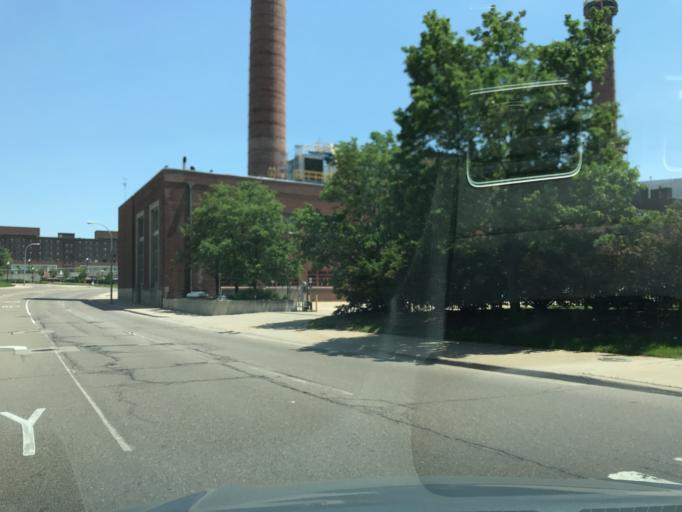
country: US
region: Michigan
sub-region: Washtenaw County
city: Ann Arbor
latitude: 42.2814
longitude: -83.7354
